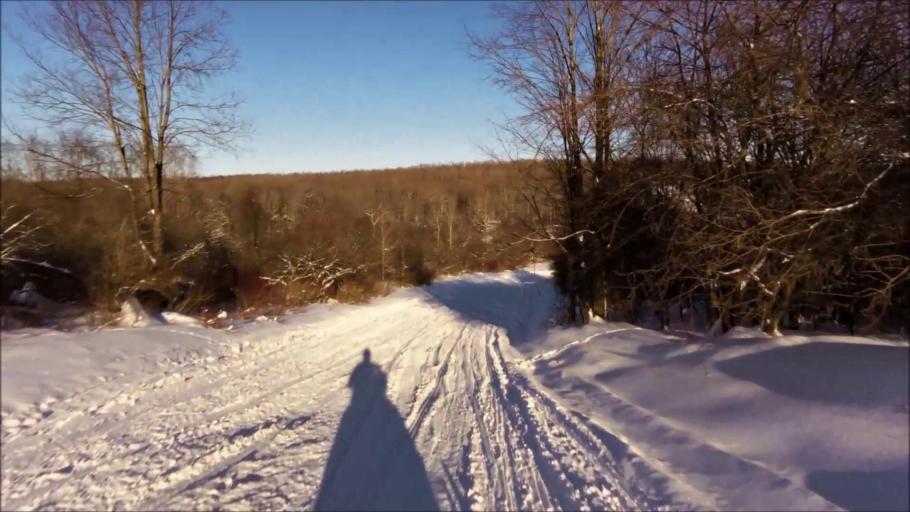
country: US
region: New York
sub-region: Chautauqua County
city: Mayville
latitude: 42.2819
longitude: -79.4225
